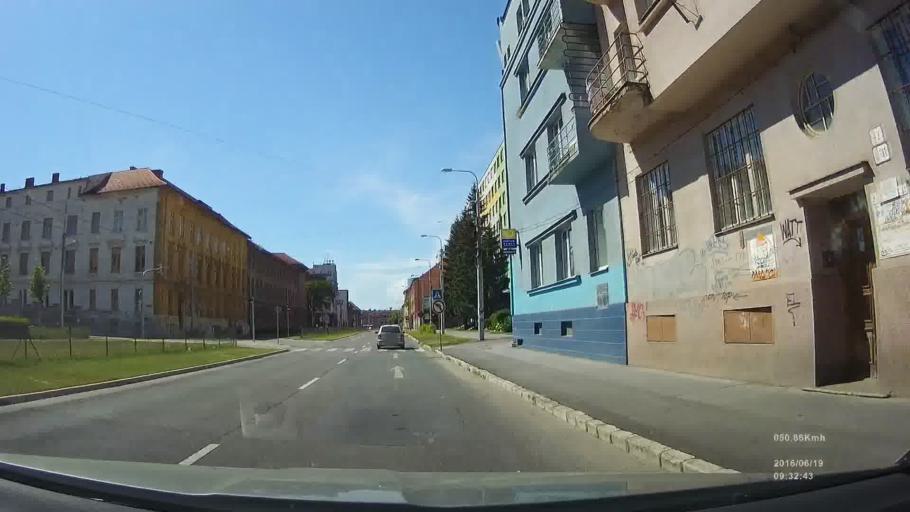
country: SK
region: Kosicky
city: Kosice
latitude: 48.7204
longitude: 21.2496
